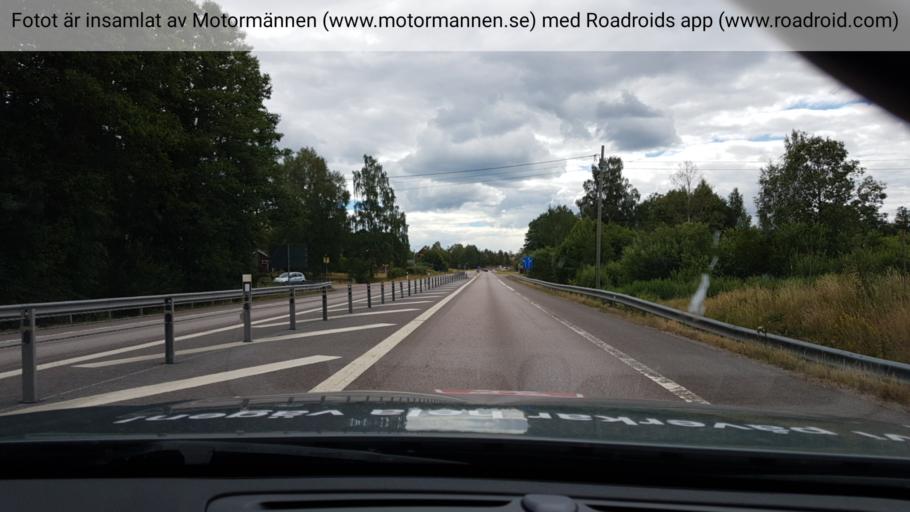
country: SE
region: Kalmar
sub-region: Oskarshamns Kommun
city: Oskarshamn
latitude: 57.4121
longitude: 16.4819
